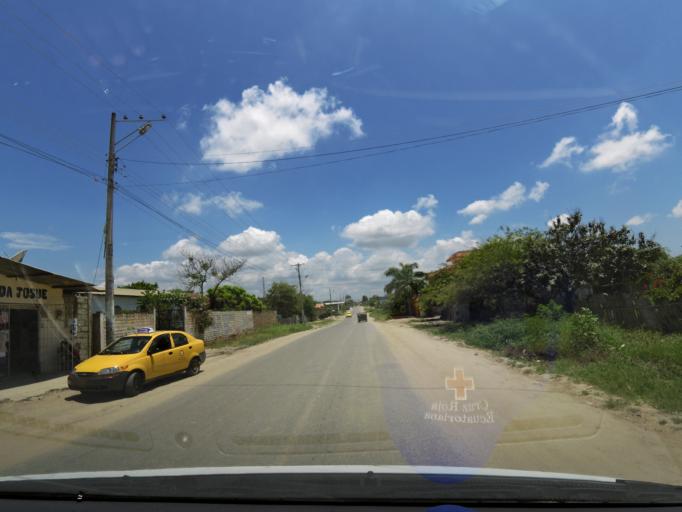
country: EC
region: El Oro
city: Huaquillas
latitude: -3.4801
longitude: -80.2110
